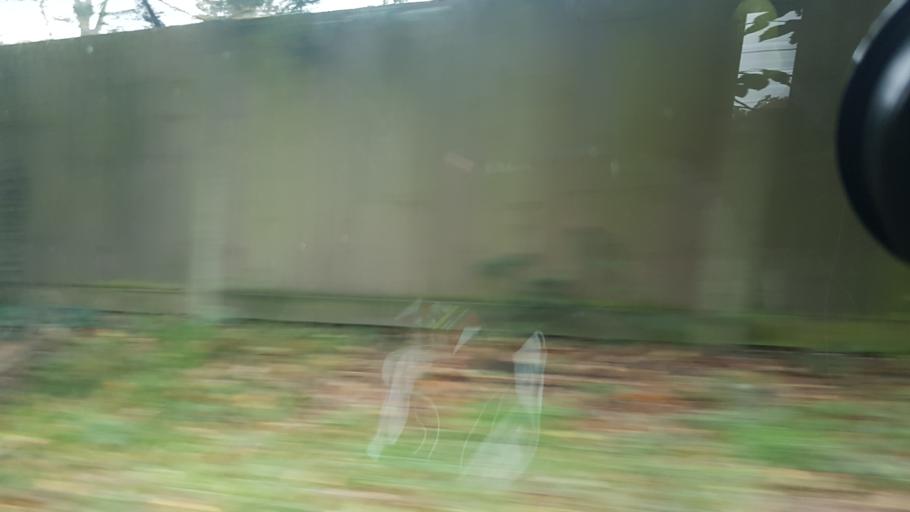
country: GB
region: England
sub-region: Hampshire
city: Eversley
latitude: 51.3478
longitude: -0.8829
